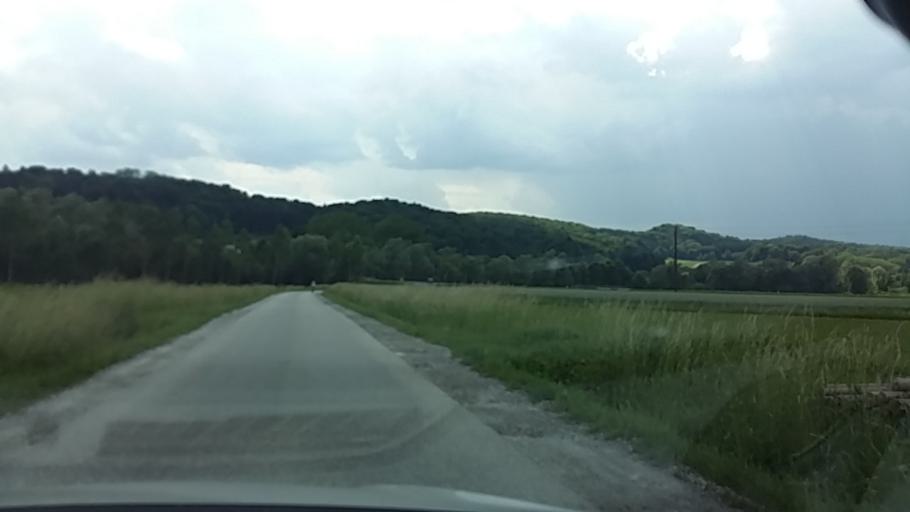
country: AT
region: Styria
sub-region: Politischer Bezirk Hartberg-Fuerstenfeld
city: Soechau
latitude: 47.0641
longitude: 16.0112
